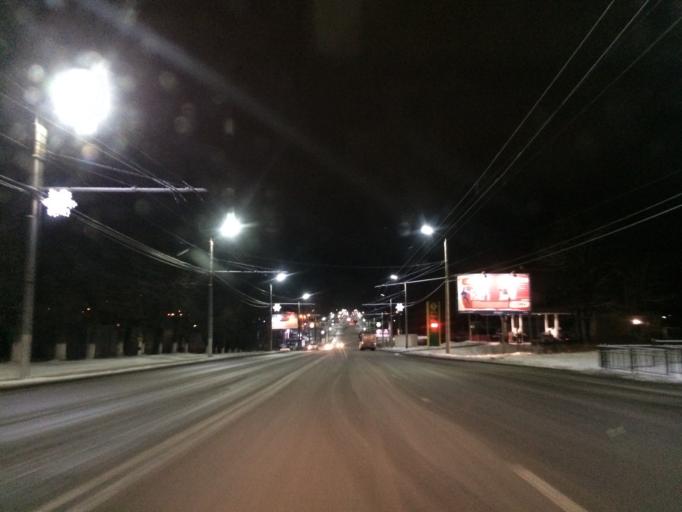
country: RU
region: Tula
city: Gorelki
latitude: 54.2424
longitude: 37.6176
